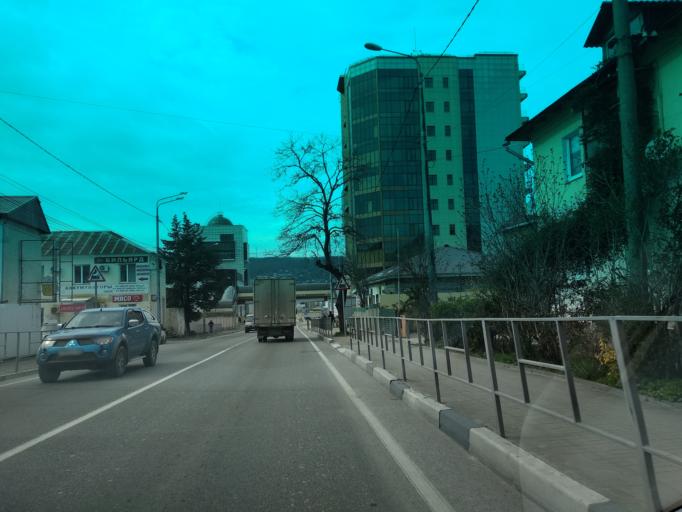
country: RU
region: Krasnodarskiy
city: Tuapse
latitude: 44.0988
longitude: 39.0973
